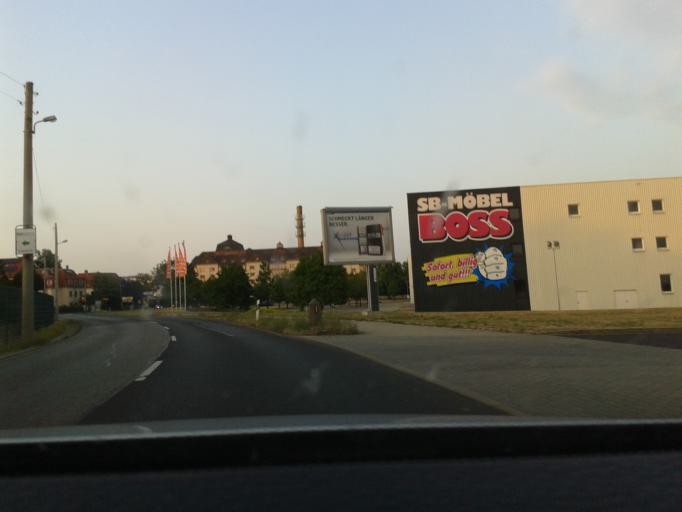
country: DE
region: Saxony
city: Heidenau
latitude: 51.0072
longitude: 13.8098
